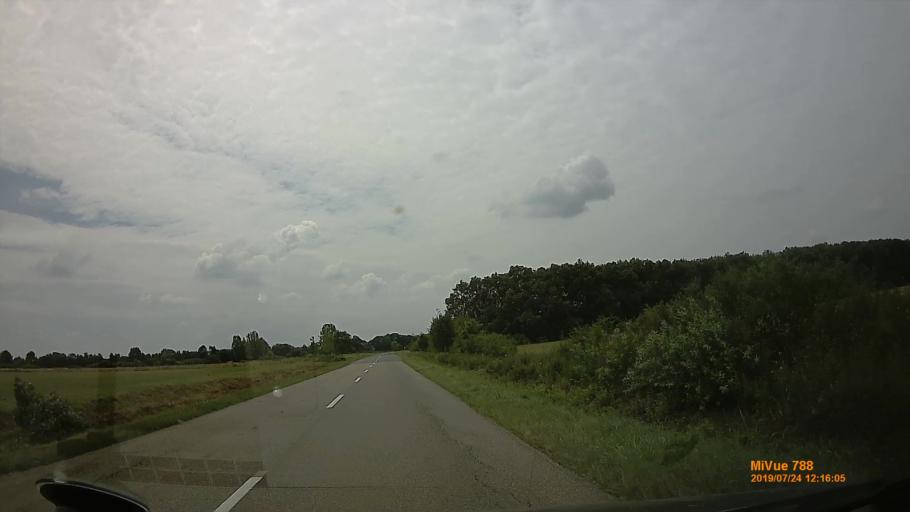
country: HU
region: Szabolcs-Szatmar-Bereg
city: Vasarosnameny
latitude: 48.1766
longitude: 22.3452
